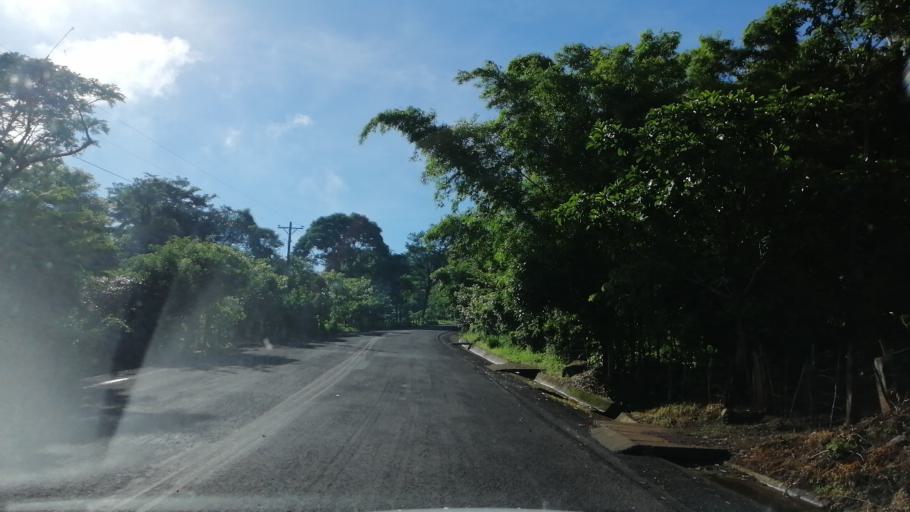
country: SV
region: Morazan
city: Cacaopera
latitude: 13.7727
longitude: -88.0907
